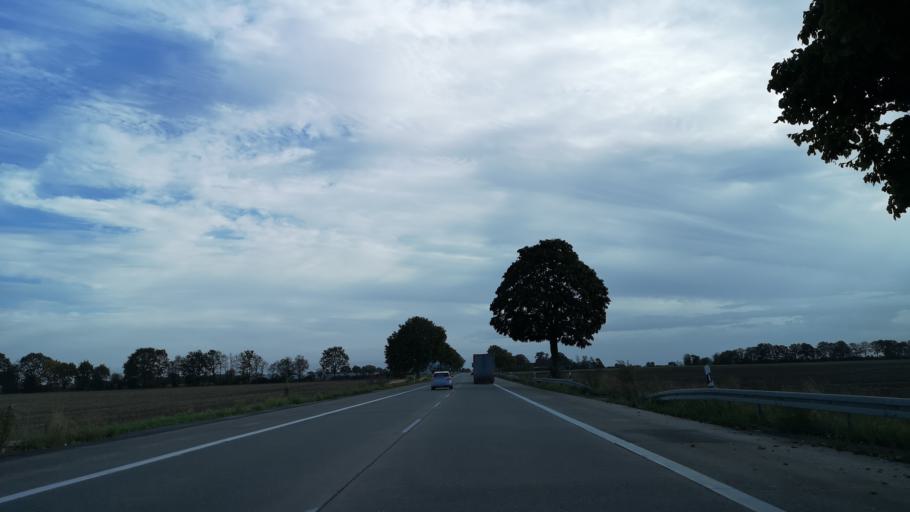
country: DE
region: North Rhine-Westphalia
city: Erwitte
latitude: 51.6251
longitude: 8.4150
